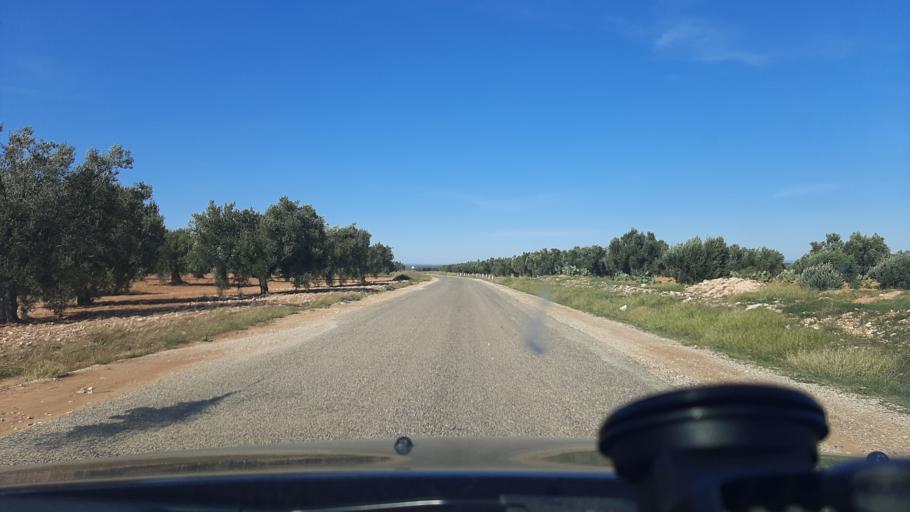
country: TN
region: Safaqis
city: Sfax
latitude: 34.9645
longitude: 10.5387
